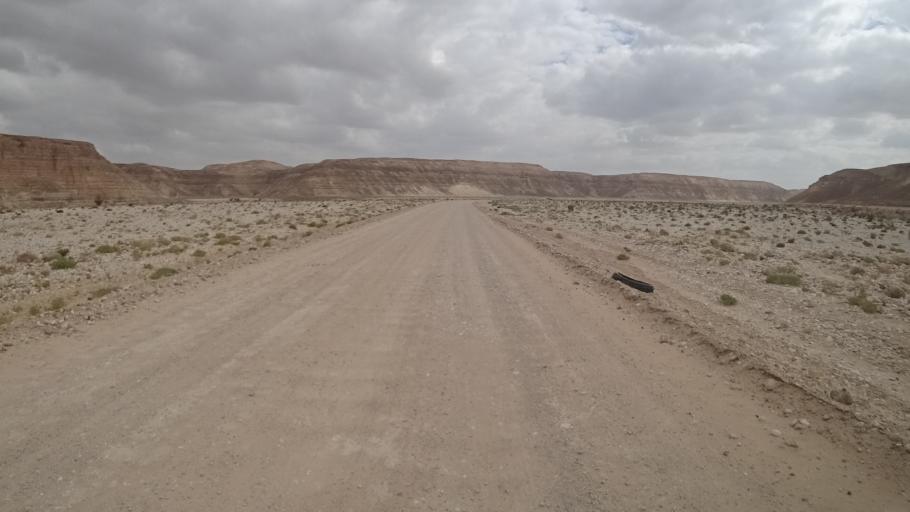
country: YE
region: Al Mahrah
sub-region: Shahan
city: Shihan as Sufla
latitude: 17.4703
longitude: 53.0030
